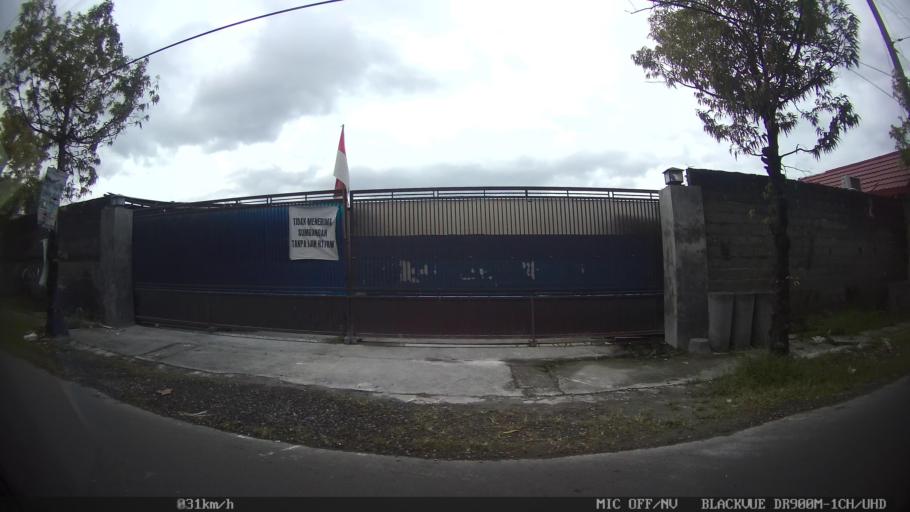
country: ID
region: Daerah Istimewa Yogyakarta
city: Depok
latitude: -7.8210
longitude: 110.4153
